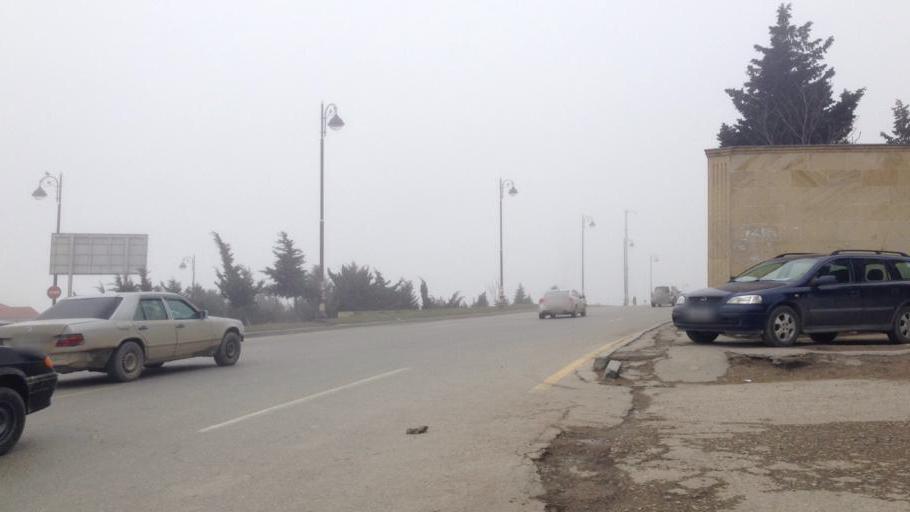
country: AZ
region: Baki
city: Qaracuxur
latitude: 40.3489
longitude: 49.9613
